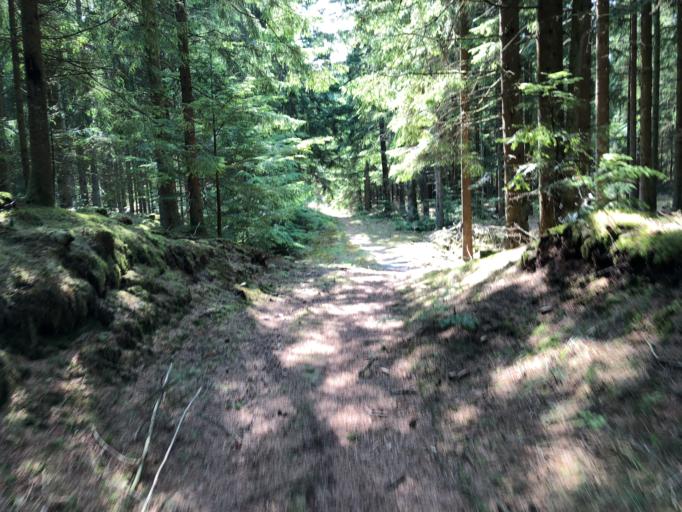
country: DK
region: Central Jutland
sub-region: Holstebro Kommune
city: Ulfborg
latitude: 56.2504
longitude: 8.4482
